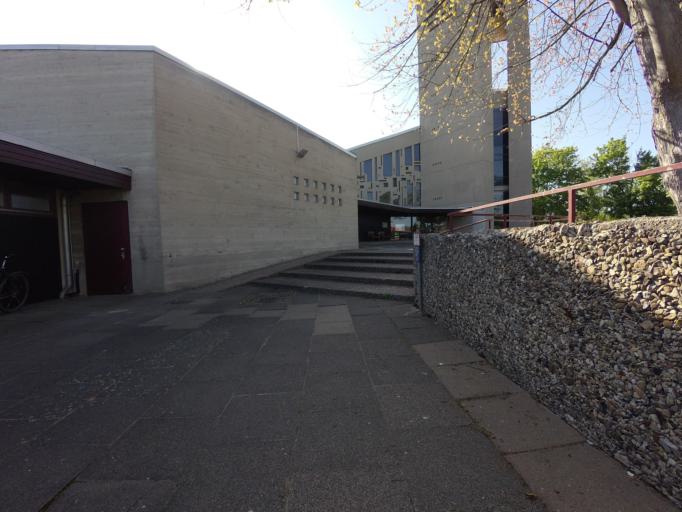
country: DE
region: Lower Saxony
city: Hildesheim
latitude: 52.1388
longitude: 9.9227
